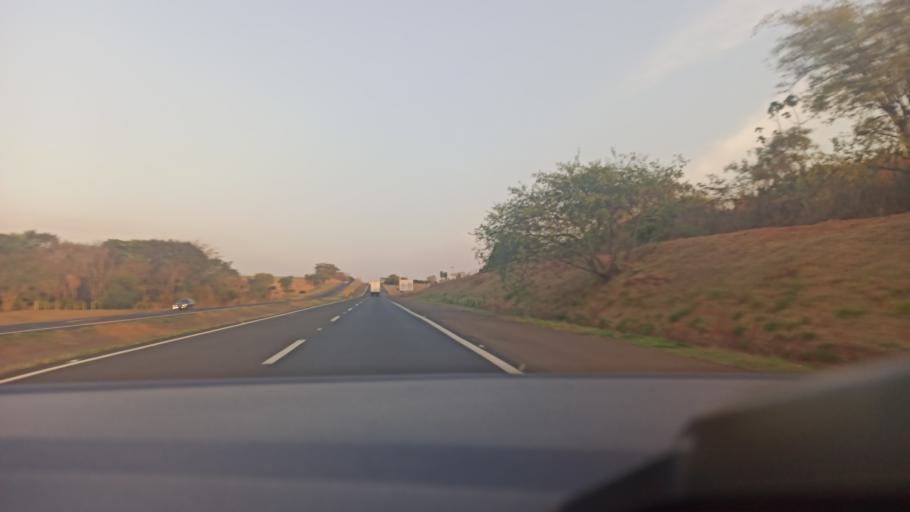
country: BR
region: Sao Paulo
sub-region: Santa Adelia
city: Santa Adelia
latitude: -21.3981
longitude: -48.7106
